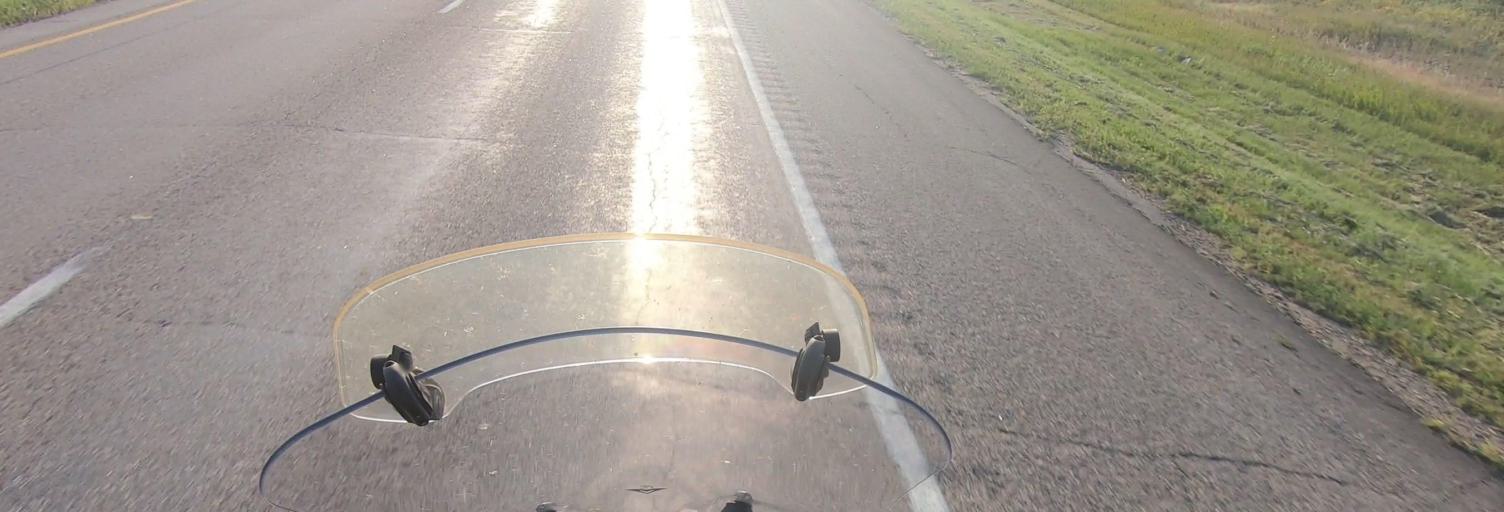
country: CA
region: Saskatchewan
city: Indian Head
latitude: 50.5276
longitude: -103.7734
